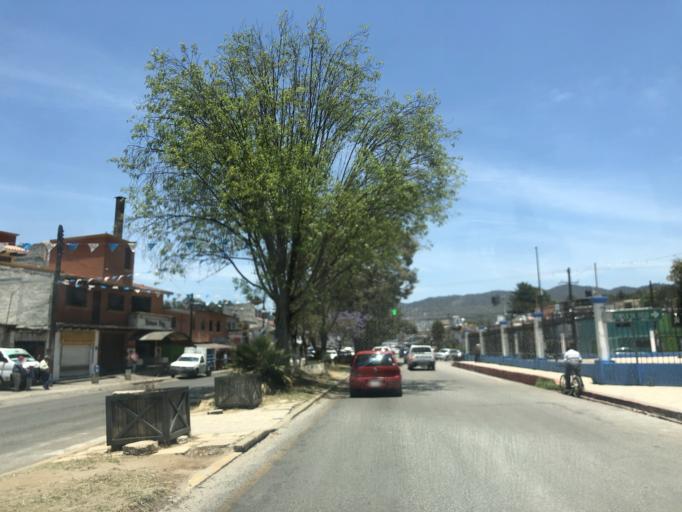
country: MX
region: Chiapas
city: San Cristobal de las Casas
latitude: 16.7264
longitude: -92.6355
